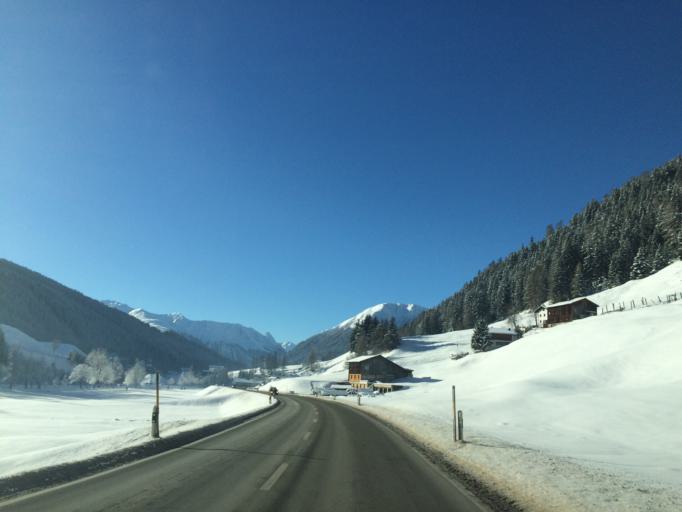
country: CH
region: Grisons
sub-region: Praettigau/Davos District
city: Davos
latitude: 46.7764
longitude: 9.8050
